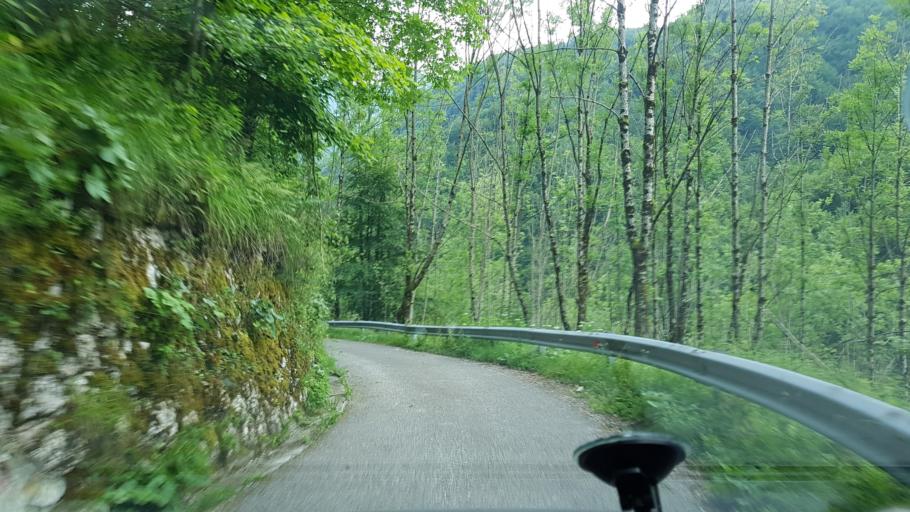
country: IT
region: Friuli Venezia Giulia
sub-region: Provincia di Udine
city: Taipana
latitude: 46.3161
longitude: 13.3920
